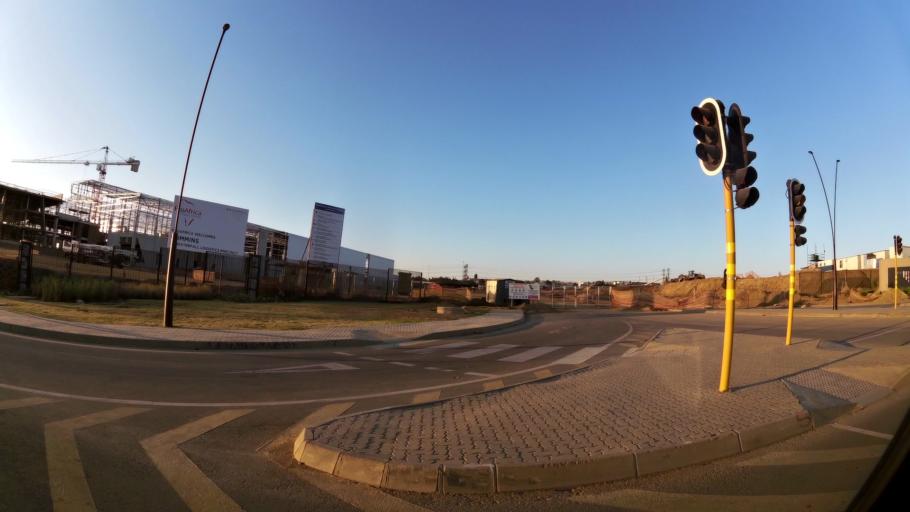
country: ZA
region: Gauteng
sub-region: City of Johannesburg Metropolitan Municipality
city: Midrand
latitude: -26.0212
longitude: 28.1157
